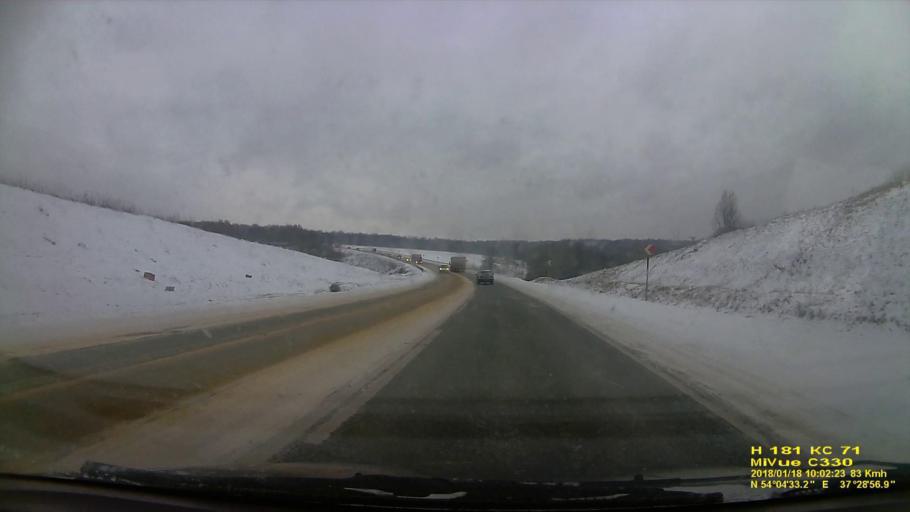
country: RU
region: Tula
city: Pervomayskiy
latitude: 54.0757
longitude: 37.4821
